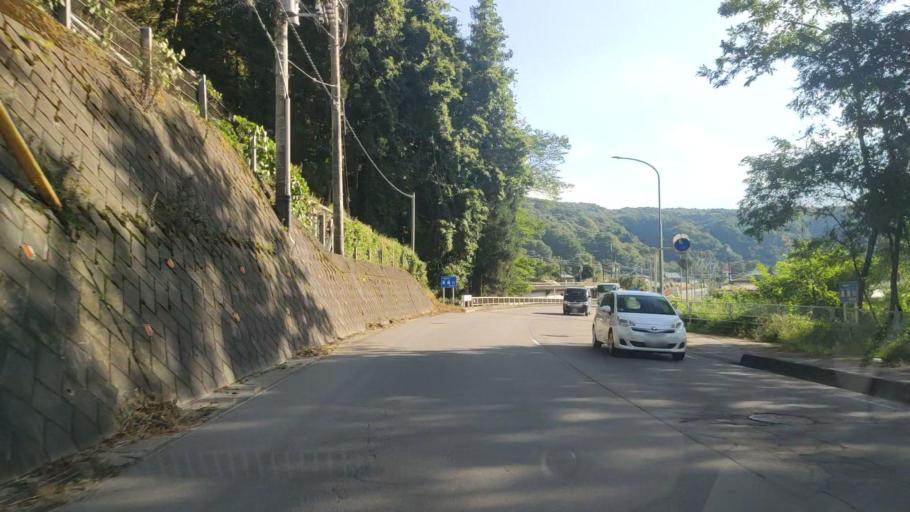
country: JP
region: Nagano
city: Komoro
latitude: 36.5246
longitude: 138.5431
